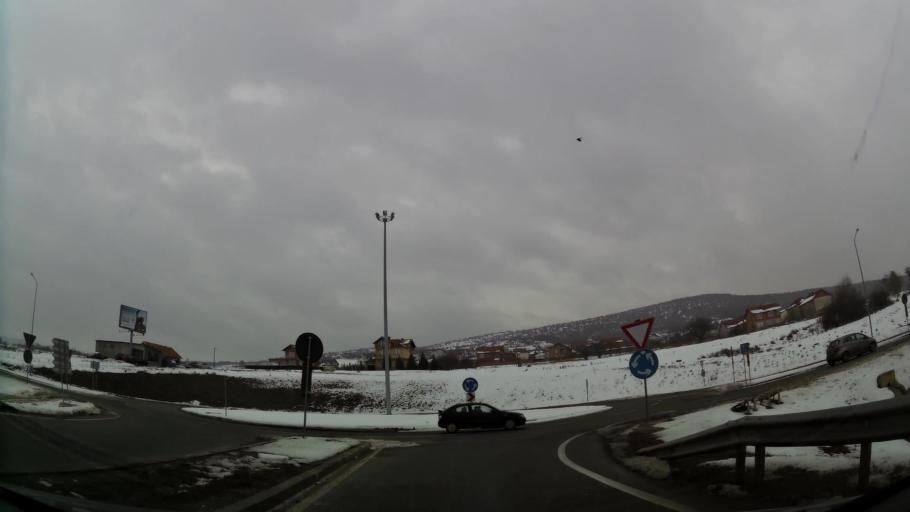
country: XK
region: Pristina
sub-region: Komuna e Prishtines
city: Pristina
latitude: 42.7320
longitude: 21.1423
